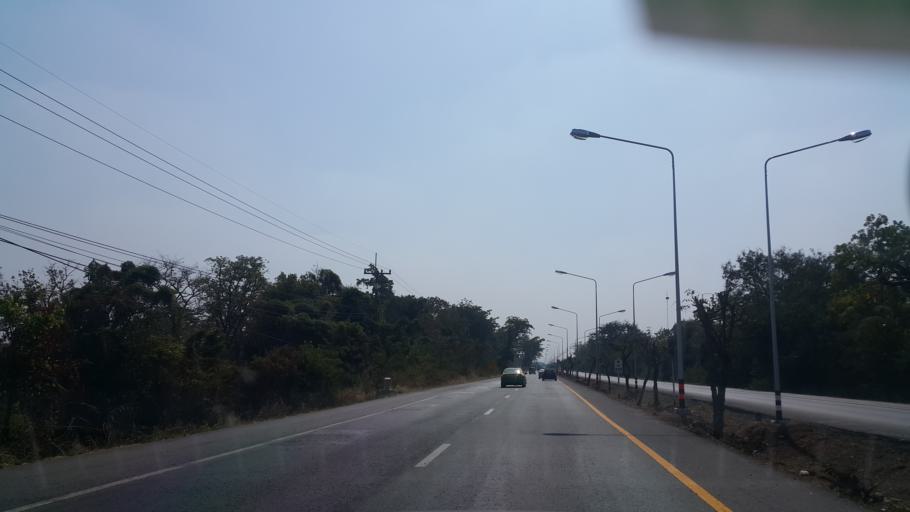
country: TH
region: Nakhon Ratchasima
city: Non Daeng
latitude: 15.3624
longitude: 102.4532
